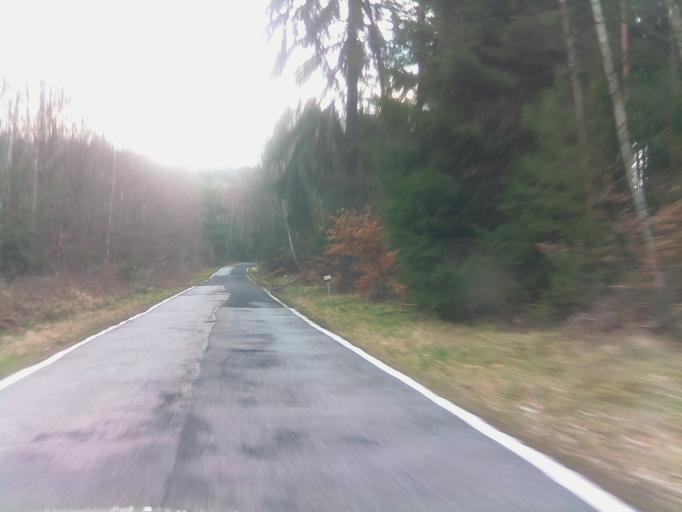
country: DE
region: Rheinland-Pfalz
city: Oberheimbach
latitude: 49.9835
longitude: 7.8003
